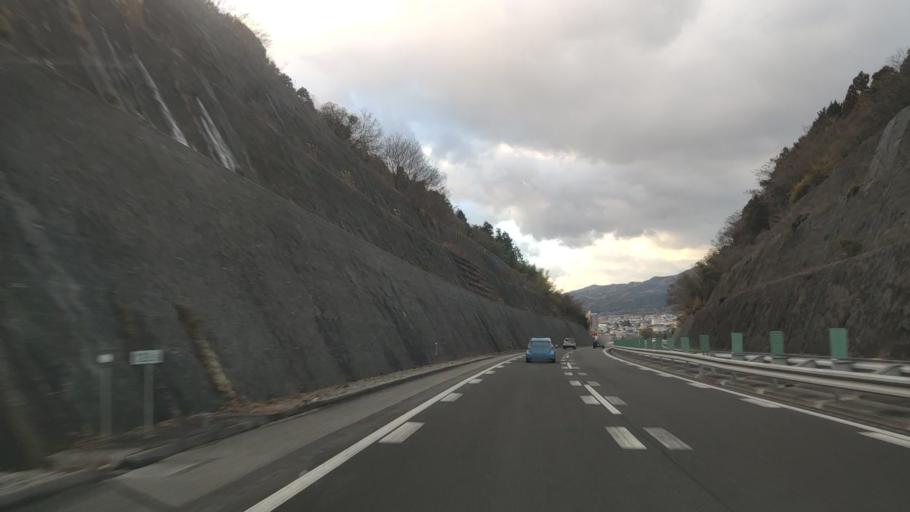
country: JP
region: Ehime
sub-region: Shikoku-chuo Shi
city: Matsuyama
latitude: 33.7913
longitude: 132.9149
